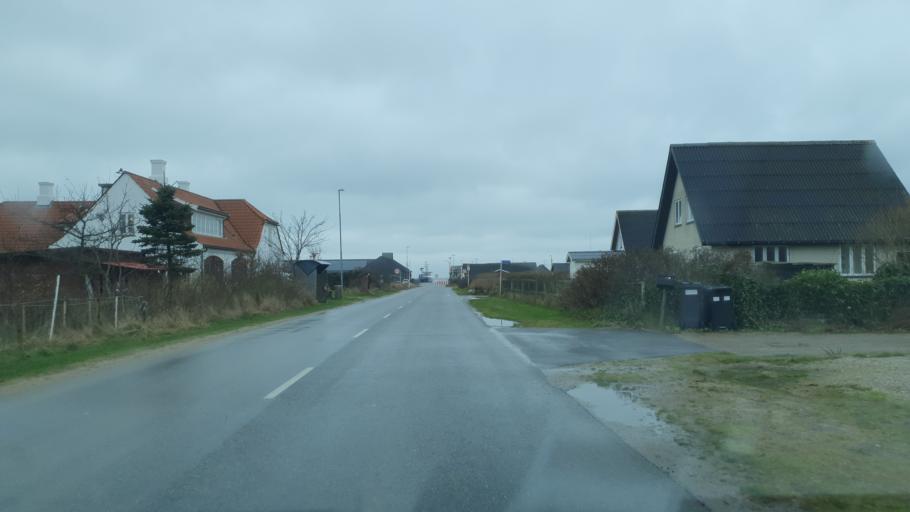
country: DK
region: North Denmark
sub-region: Jammerbugt Kommune
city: Fjerritslev
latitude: 57.1378
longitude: 9.1260
